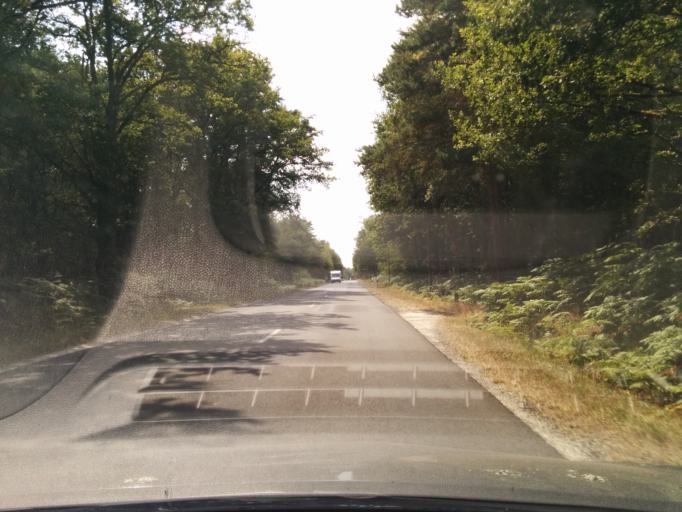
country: FR
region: Centre
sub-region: Departement du Cher
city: Neuvy-sur-Barangeon
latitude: 47.3230
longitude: 2.3033
